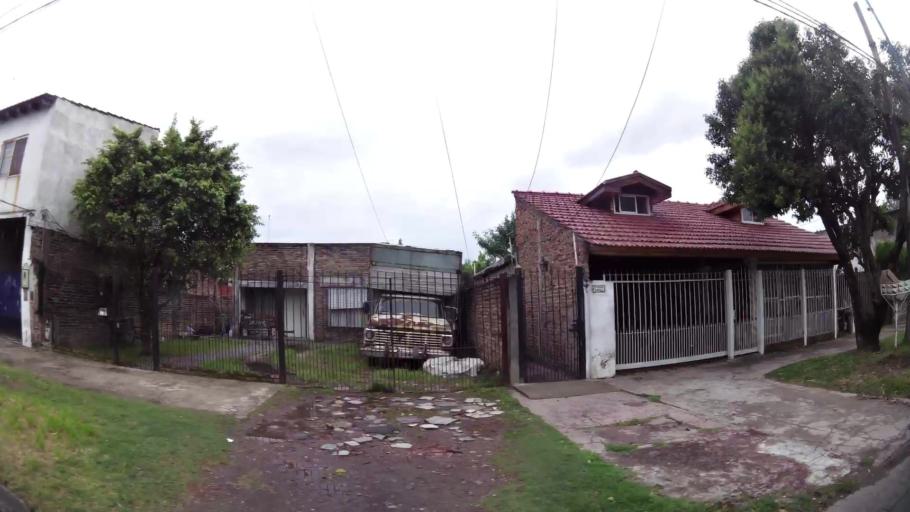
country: AR
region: Buenos Aires
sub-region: Partido de Lanus
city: Lanus
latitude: -34.7248
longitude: -58.3765
